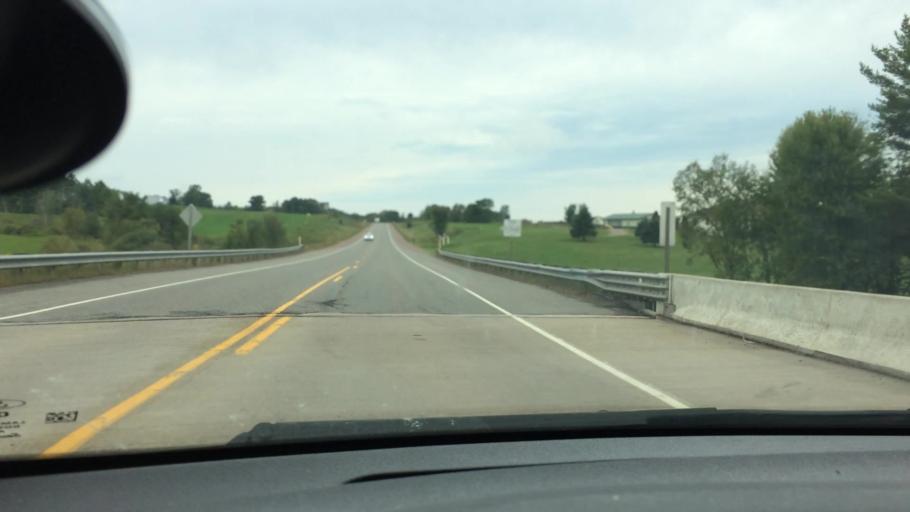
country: US
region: Wisconsin
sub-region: Clark County
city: Neillsville
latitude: 44.5523
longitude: -90.6091
